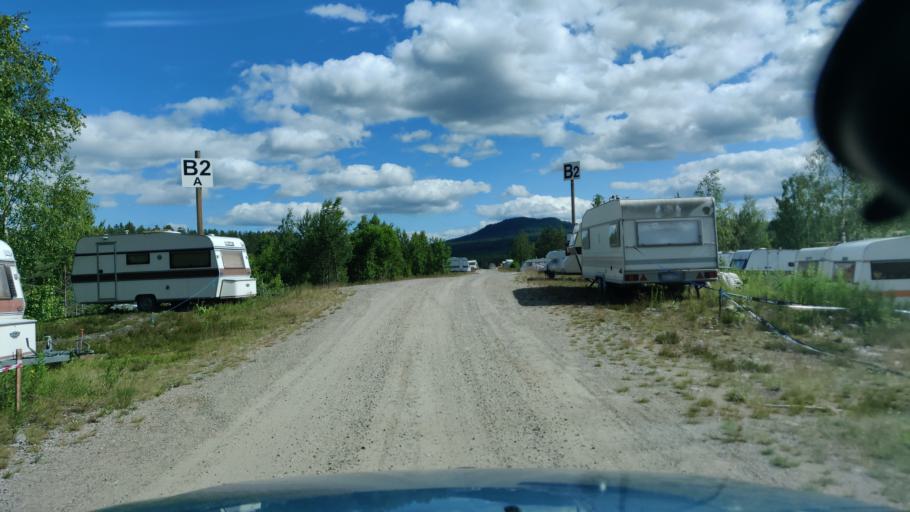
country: NO
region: Hedmark
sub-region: Trysil
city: Innbygda
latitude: 60.9120
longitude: 12.5616
